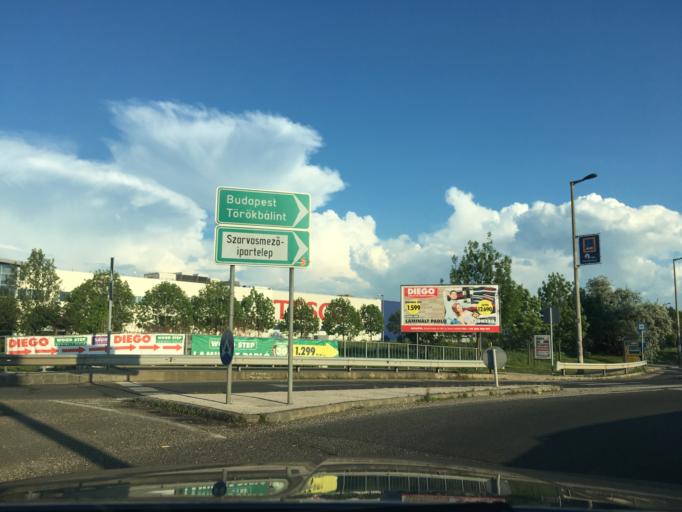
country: HU
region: Pest
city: Budaors
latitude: 47.4506
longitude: 18.9623
